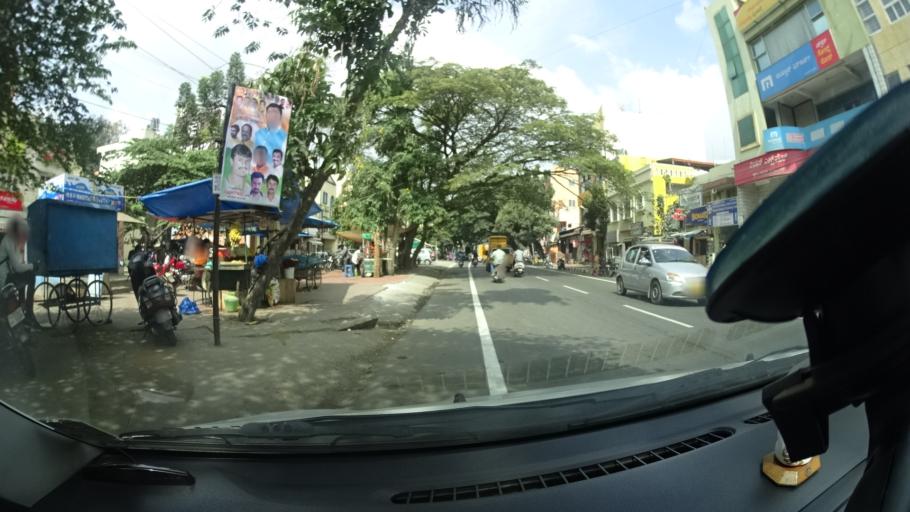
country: IN
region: Karnataka
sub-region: Bangalore Urban
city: Yelahanka
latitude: 13.0962
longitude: 77.5789
